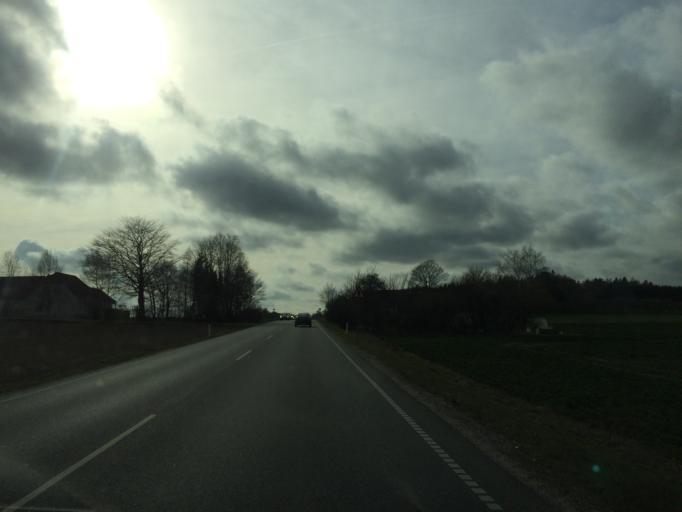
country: DK
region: Central Jutland
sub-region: Norddjurs Kommune
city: Allingabro
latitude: 56.4449
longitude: 10.2464
